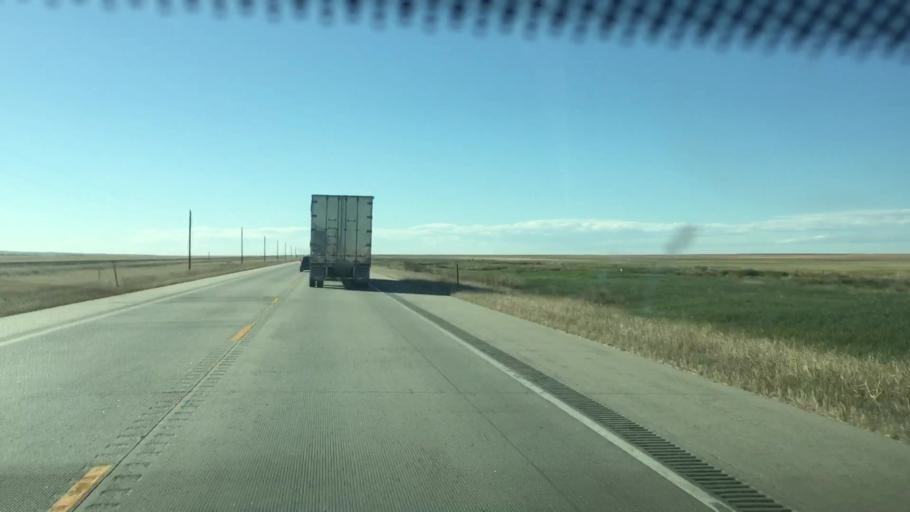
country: US
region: Colorado
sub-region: Kiowa County
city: Eads
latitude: 38.8322
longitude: -103.0508
